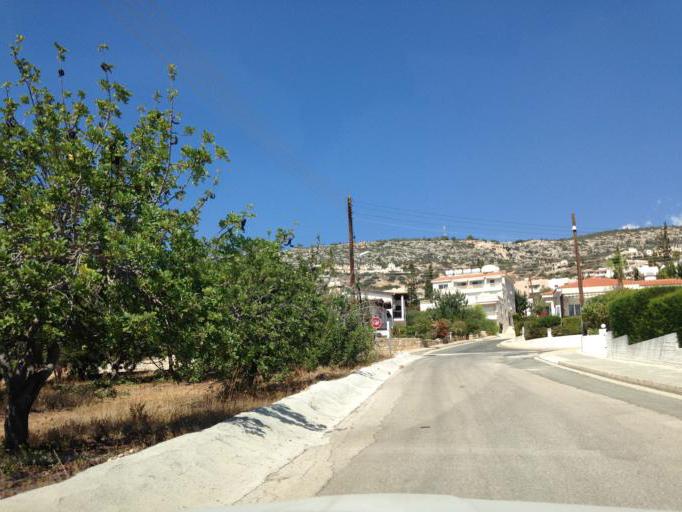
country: CY
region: Pafos
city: Pegeia
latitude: 34.8810
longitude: 32.3755
